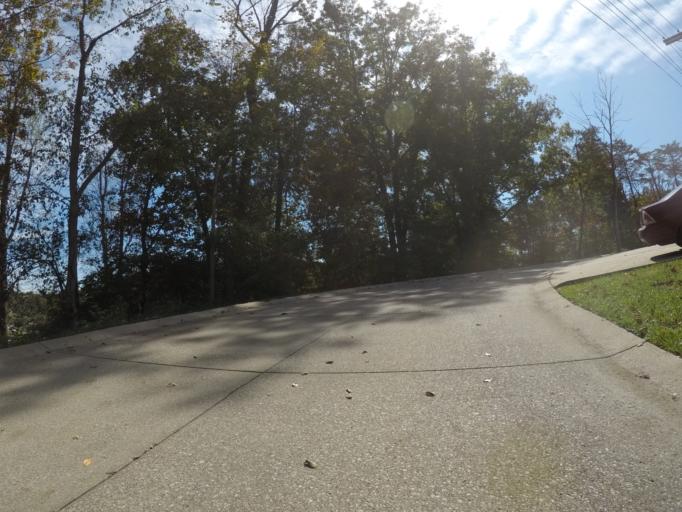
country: US
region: West Virginia
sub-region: Cabell County
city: Huntington
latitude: 38.3942
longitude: -82.3874
